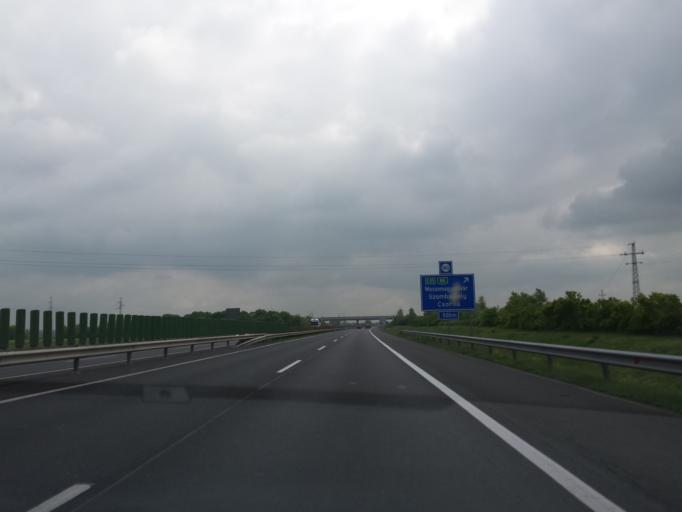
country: HU
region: Gyor-Moson-Sopron
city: Mosonmagyarovar
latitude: 47.8607
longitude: 17.2358
